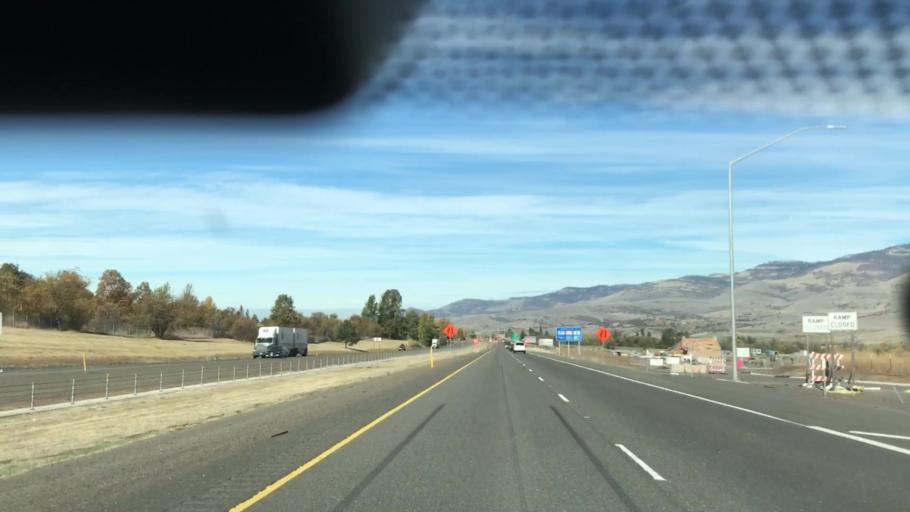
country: US
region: Oregon
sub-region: Jackson County
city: Ashland
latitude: 42.1632
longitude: -122.6511
